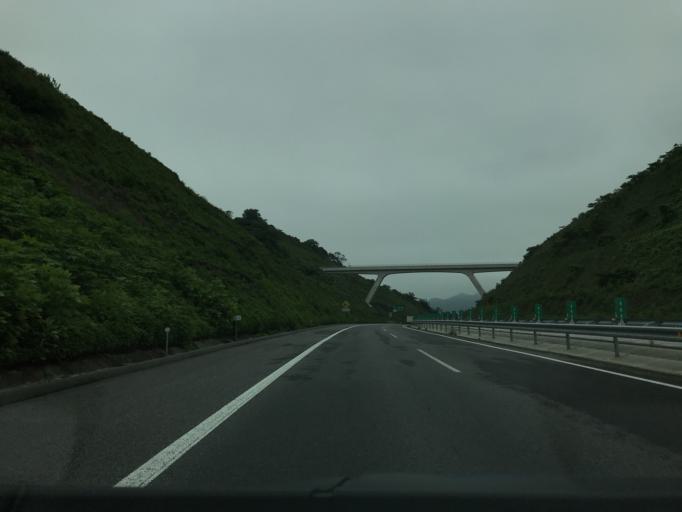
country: JP
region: Oita
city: Bungo-Takada-shi
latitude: 33.5041
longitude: 131.3057
